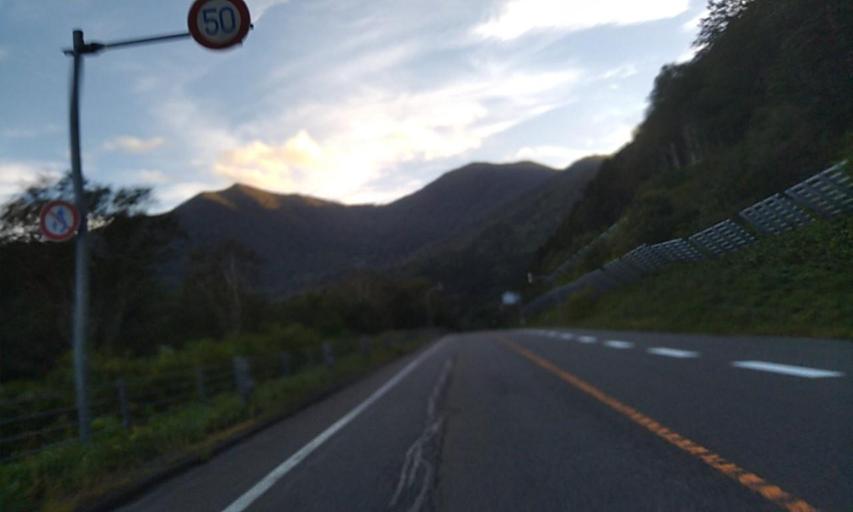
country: JP
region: Hokkaido
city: Otofuke
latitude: 42.9641
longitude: 142.7921
